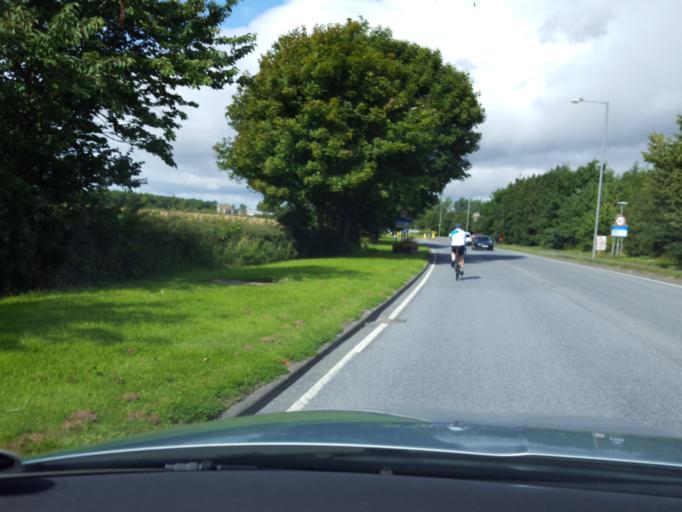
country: GB
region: Scotland
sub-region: Falkirk
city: Bo'ness
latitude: 56.0082
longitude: -3.5810
